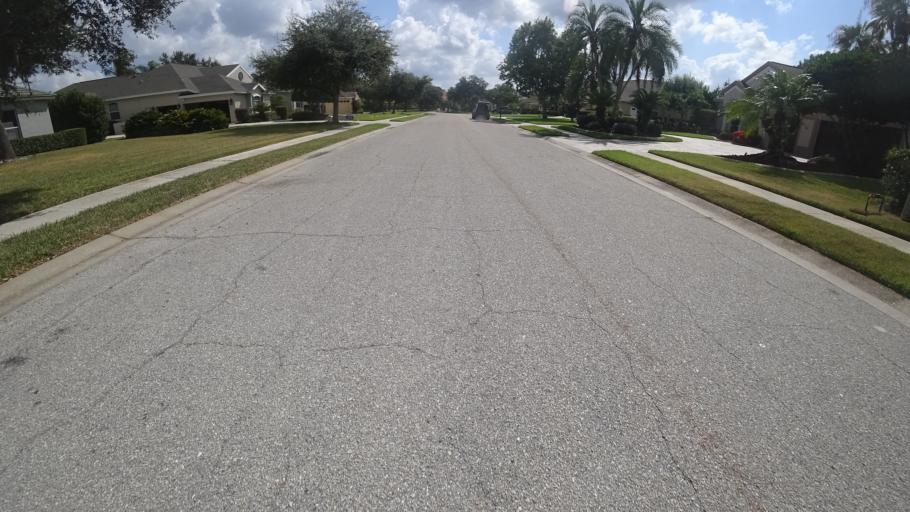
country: US
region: Florida
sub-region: Sarasota County
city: The Meadows
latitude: 27.4063
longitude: -82.4343
